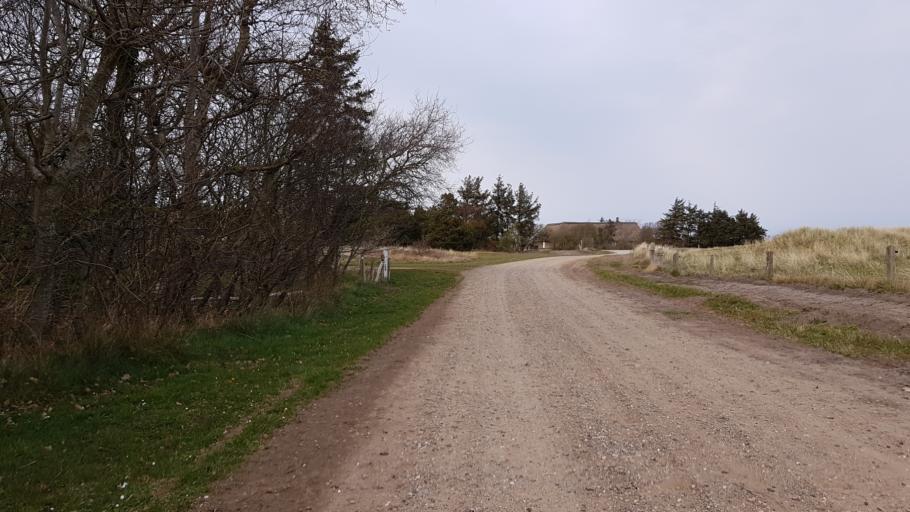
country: DE
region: Schleswig-Holstein
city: List
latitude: 55.1704
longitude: 8.5518
